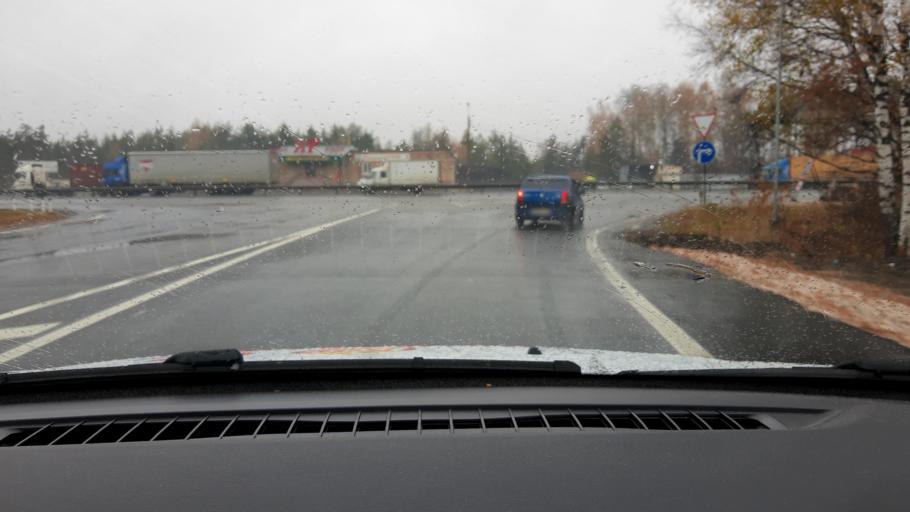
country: RU
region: Nizjnij Novgorod
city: Babino
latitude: 56.3025
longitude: 43.5913
